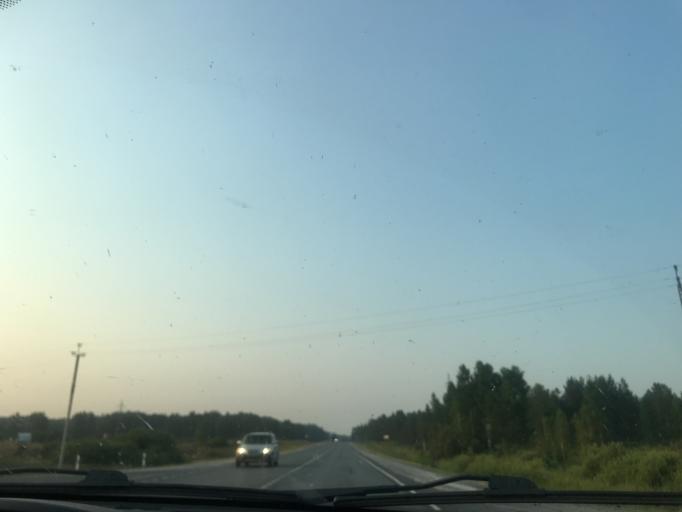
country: RU
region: Novosibirsk
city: Dorogino
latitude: 54.3750
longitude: 83.3053
